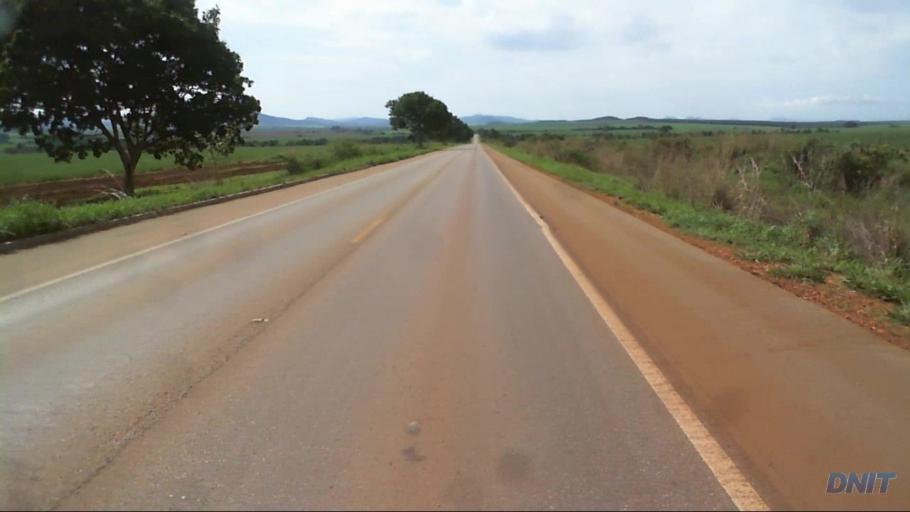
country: BR
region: Goias
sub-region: Barro Alto
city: Barro Alto
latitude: -15.0329
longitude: -48.8929
